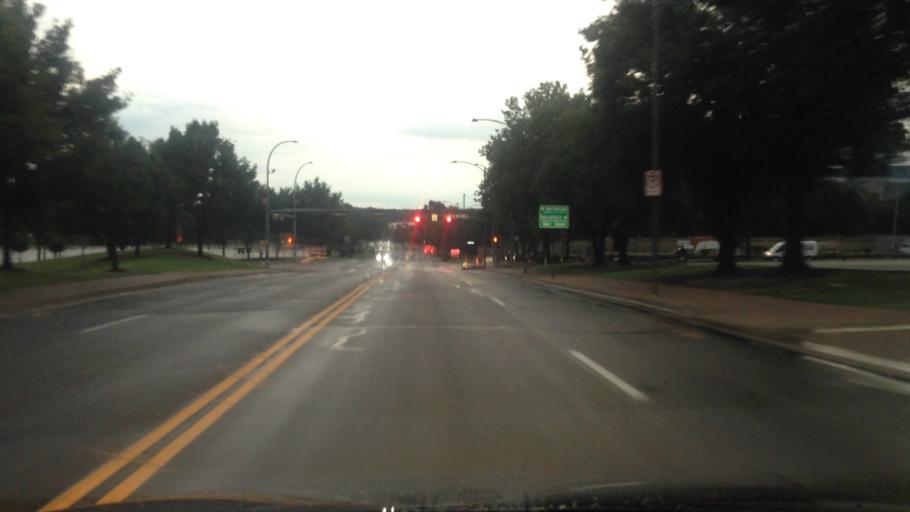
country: US
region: Texas
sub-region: Tarrant County
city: Arlington
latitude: 32.7565
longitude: -97.0887
